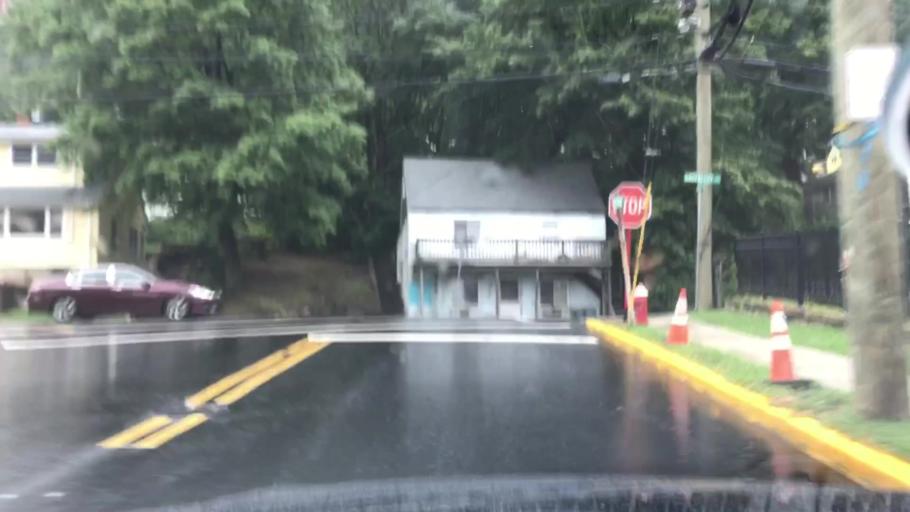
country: US
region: New Jersey
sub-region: Bergen County
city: Edgewater
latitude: 40.8214
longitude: -73.9790
